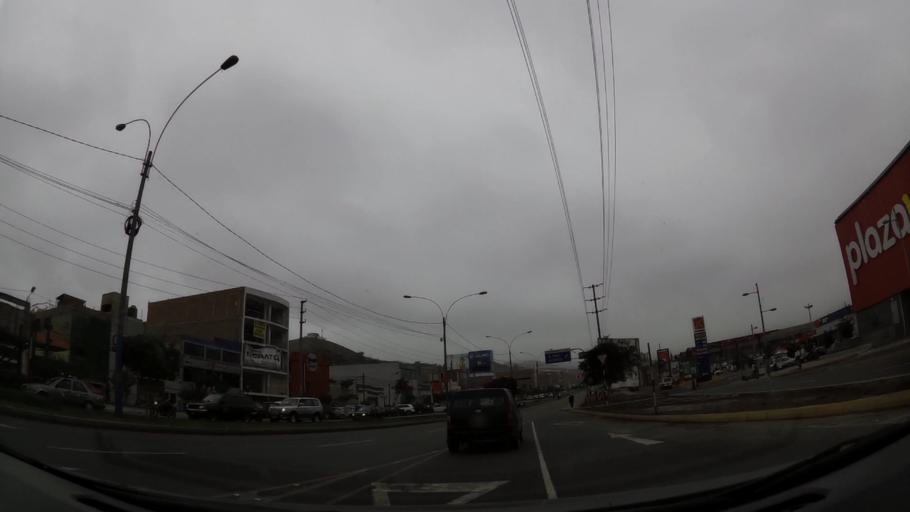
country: PE
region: Lima
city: Ventanilla
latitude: -11.8726
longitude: -77.1272
